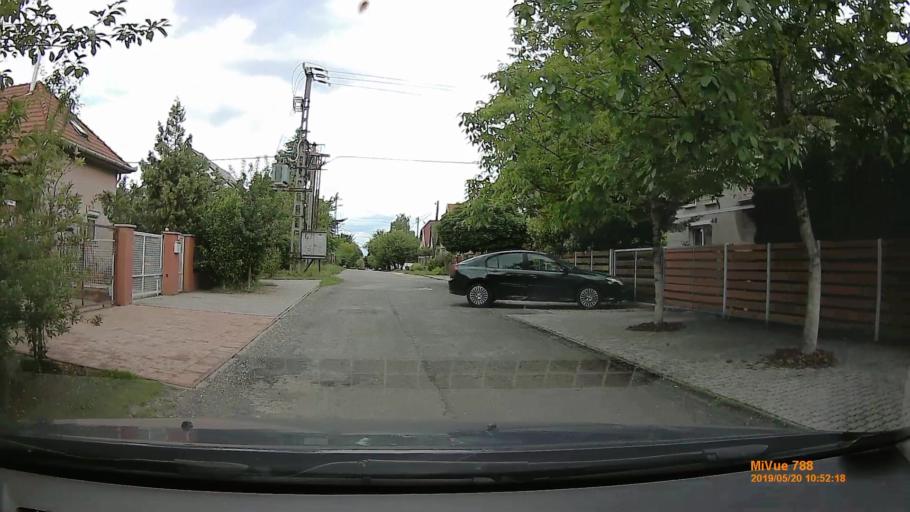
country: HU
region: Budapest
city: Budapest XVII. keruelet
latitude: 47.4999
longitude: 19.2639
